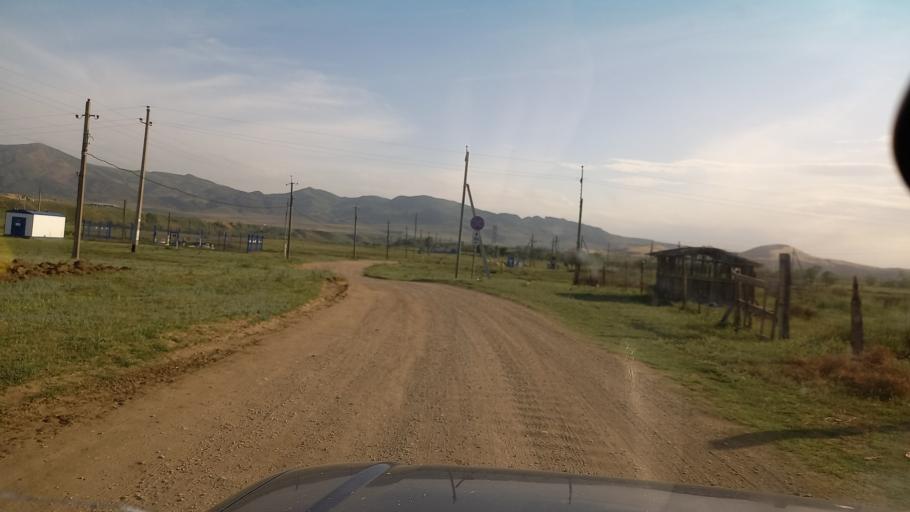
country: RU
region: Dagestan
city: Korkmaskala
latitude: 43.0252
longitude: 47.2645
